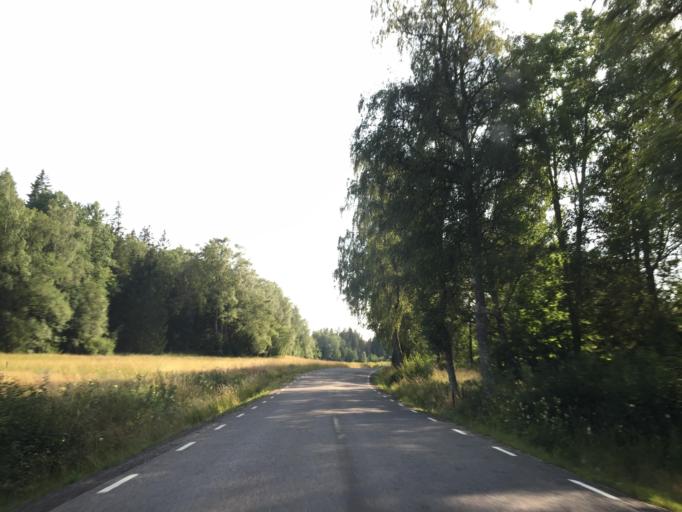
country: SE
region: Vaestra Goetaland
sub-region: Trollhattan
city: Trollhattan
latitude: 58.2687
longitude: 12.2432
